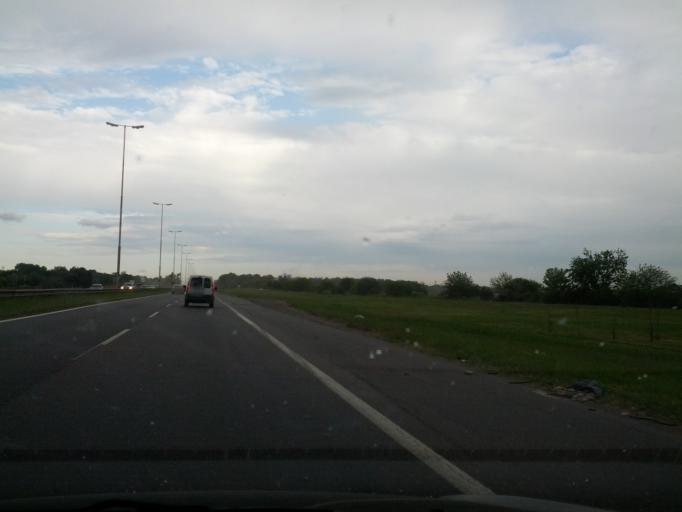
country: AR
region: Buenos Aires
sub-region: Partido de Lujan
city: Lujan
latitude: -34.5750
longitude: -59.0318
